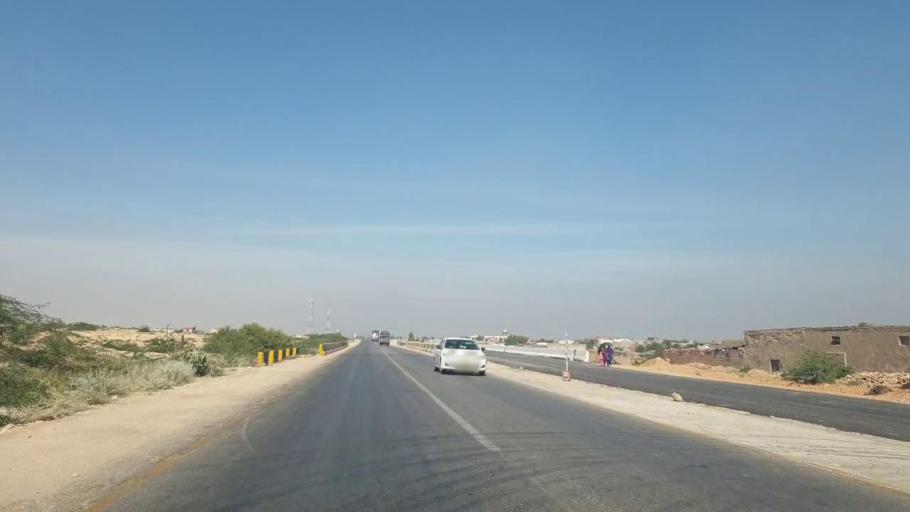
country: PK
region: Sindh
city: Hala
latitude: 25.6952
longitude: 68.2955
